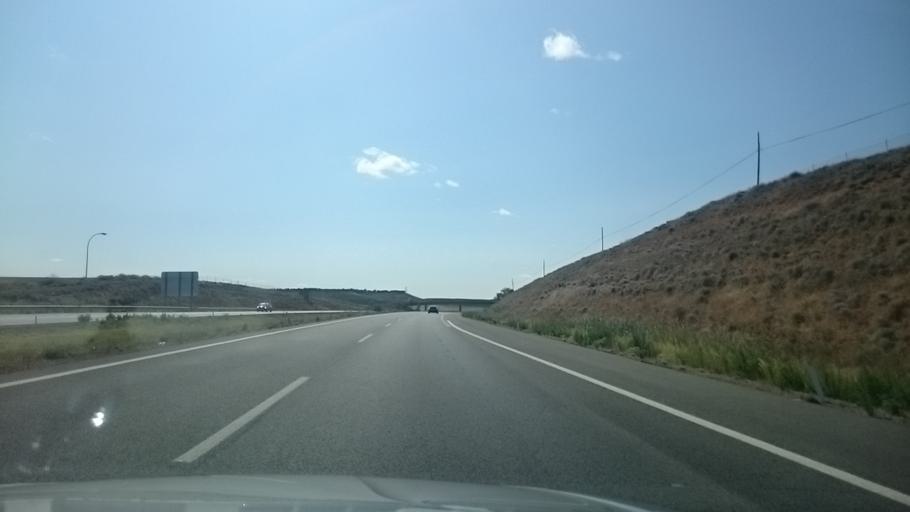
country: ES
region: Navarre
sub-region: Provincia de Navarra
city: Fontellas
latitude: 42.0110
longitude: -1.5946
